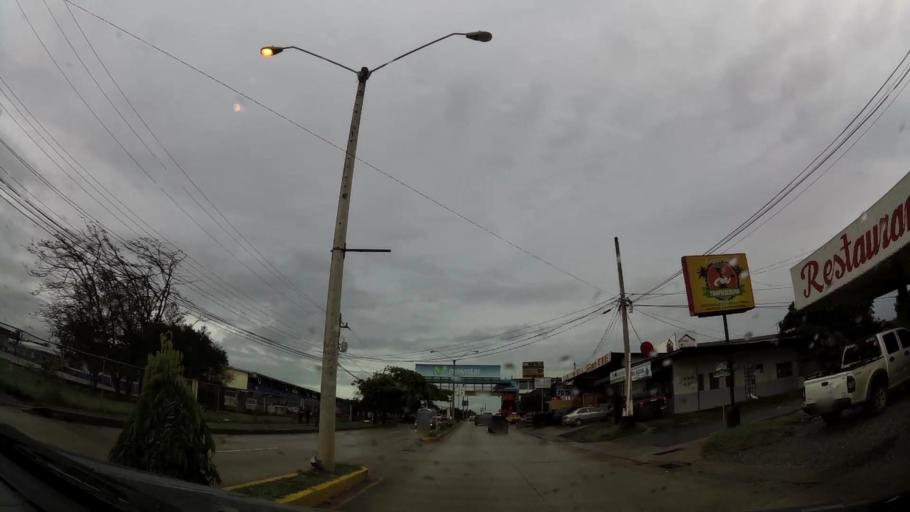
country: PA
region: Veraguas
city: Santiago de Veraguas
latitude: 8.0982
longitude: -80.9729
